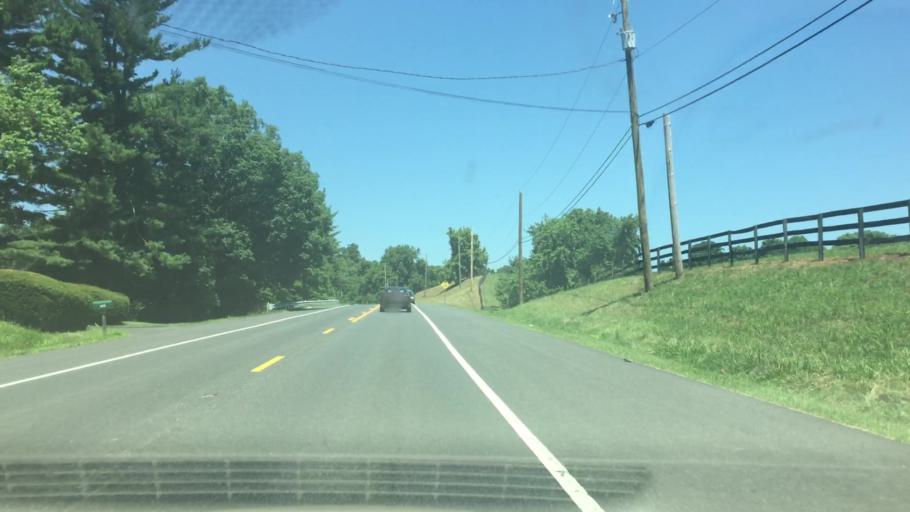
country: US
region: Maryland
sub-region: Harford County
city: Aberdeen
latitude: 39.6297
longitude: -76.2029
